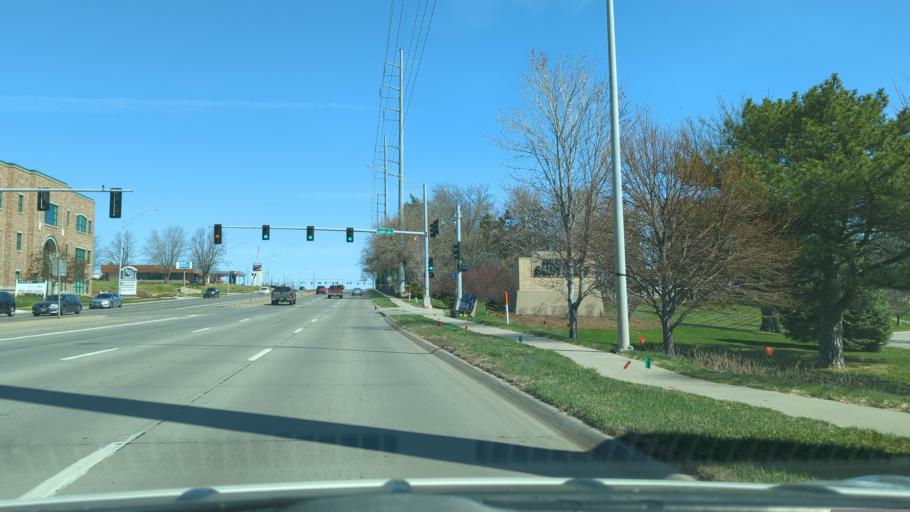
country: US
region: Nebraska
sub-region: Douglas County
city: Ralston
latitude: 41.2397
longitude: -96.0239
